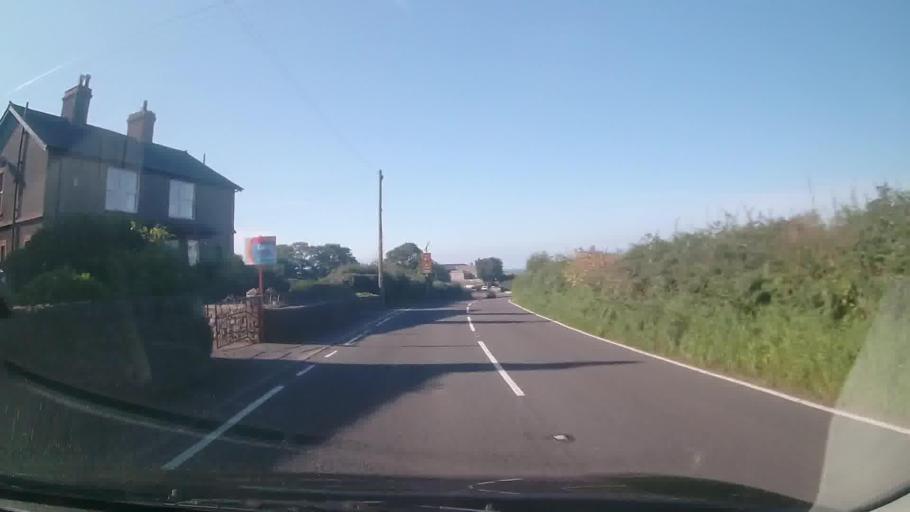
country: GB
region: England
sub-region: Cumbria
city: Seascale
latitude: 54.3289
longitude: -3.3749
